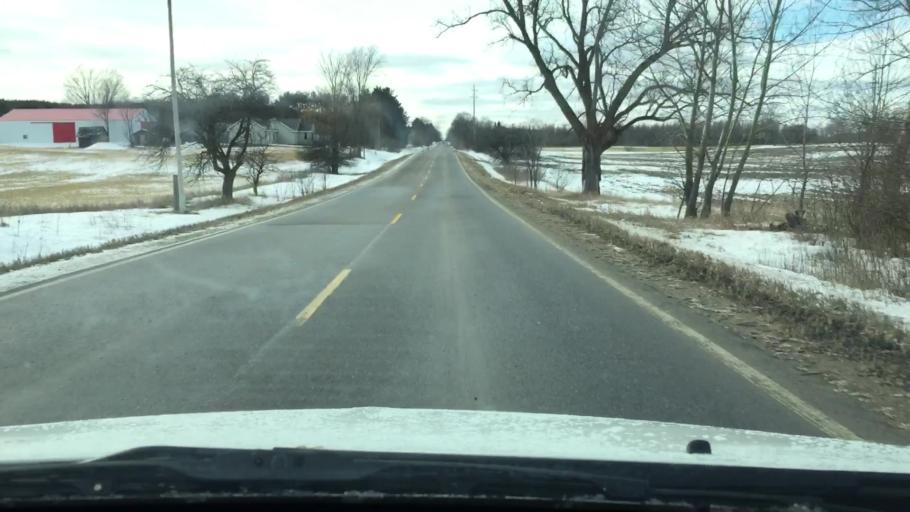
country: US
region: Michigan
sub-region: Wexford County
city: Manton
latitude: 44.4036
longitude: -85.4200
